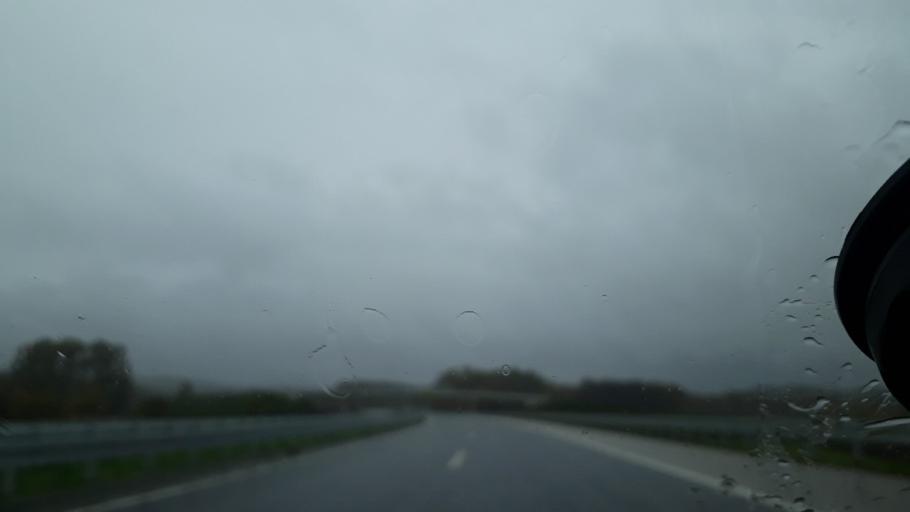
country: BA
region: Republika Srpska
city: Stanari
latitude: 44.8436
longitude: 17.7939
